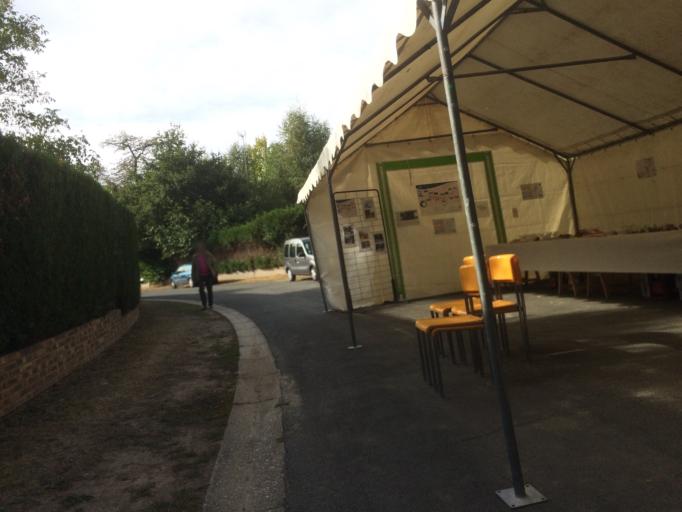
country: FR
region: Ile-de-France
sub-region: Departement des Yvelines
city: Bonnelles
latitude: 48.6252
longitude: 2.0222
